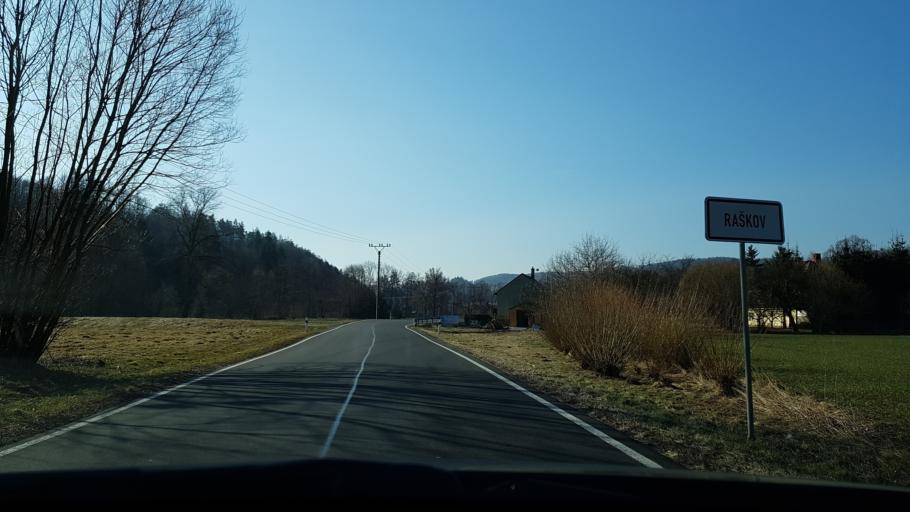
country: CZ
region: Olomoucky
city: Dolni Bohdikov
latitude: 50.0330
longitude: 16.9052
